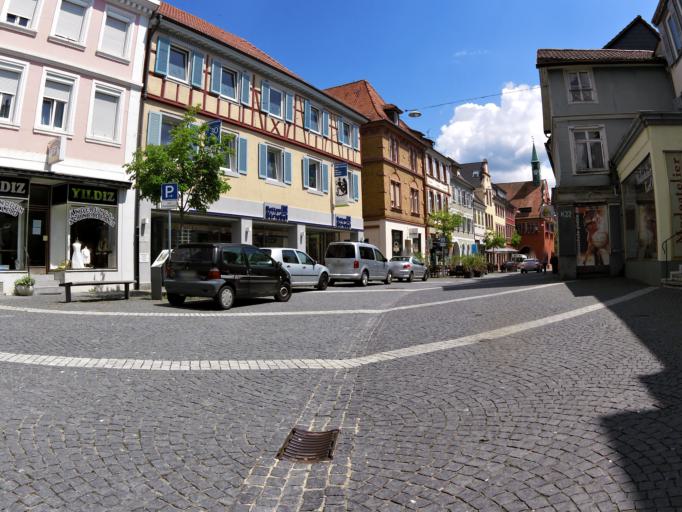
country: DE
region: Baden-Wuerttemberg
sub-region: Freiburg Region
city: Lahr
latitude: 48.3417
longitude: 7.8715
